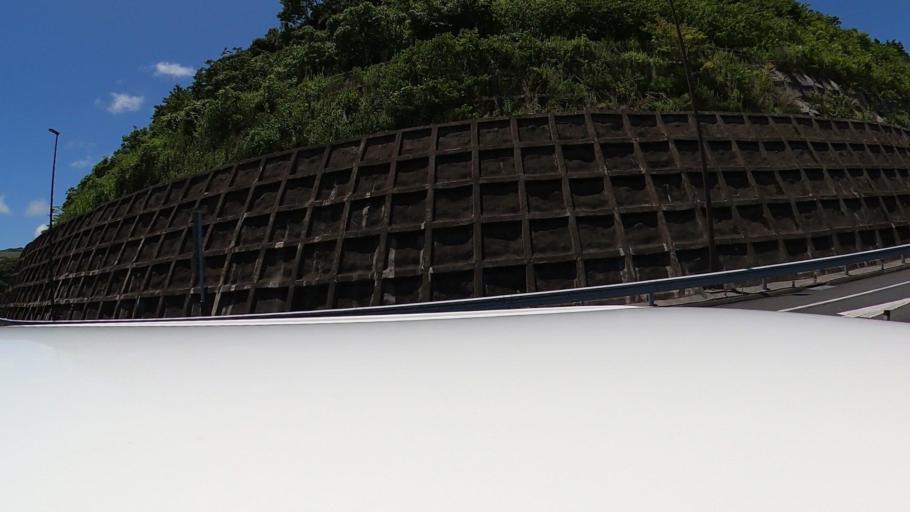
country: JP
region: Miyazaki
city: Nobeoka
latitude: 32.4022
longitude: 131.6159
